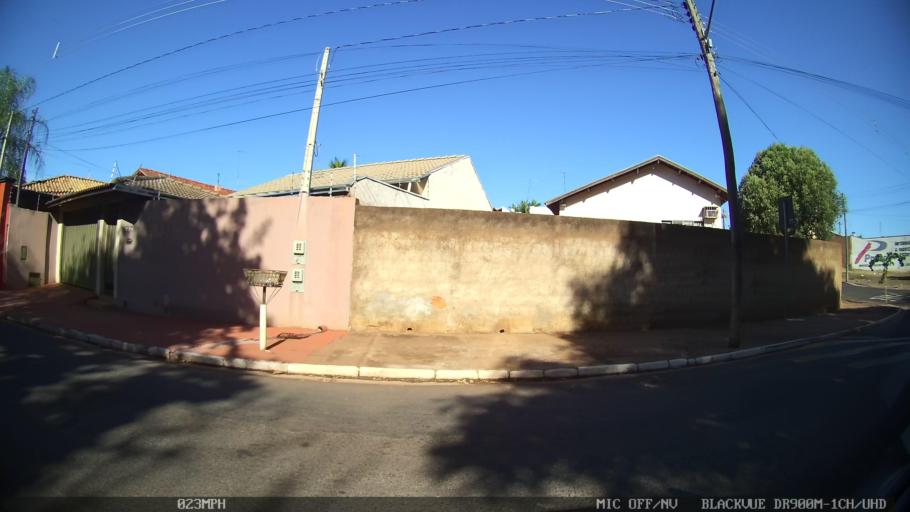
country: BR
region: Sao Paulo
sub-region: Olimpia
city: Olimpia
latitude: -20.7302
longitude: -48.9191
